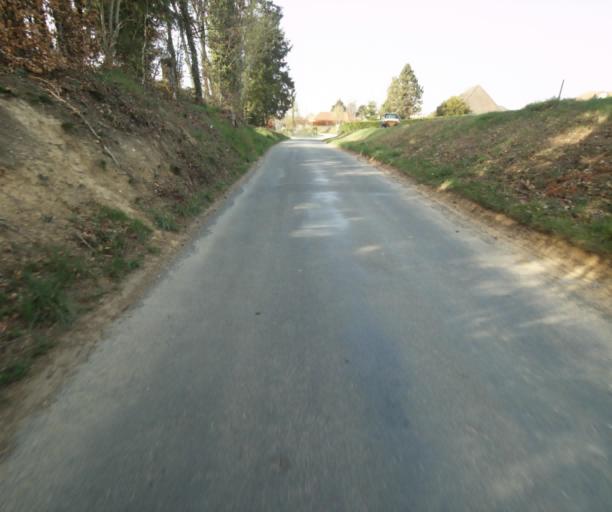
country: FR
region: Limousin
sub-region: Departement de la Correze
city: Naves
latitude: 45.2922
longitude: 1.7407
